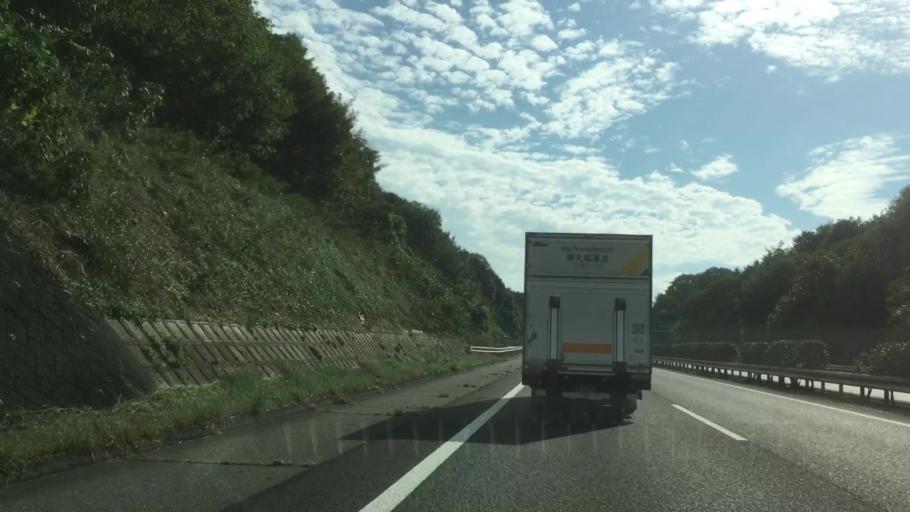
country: JP
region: Yamaguchi
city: Yanai
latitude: 34.0755
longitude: 132.0690
